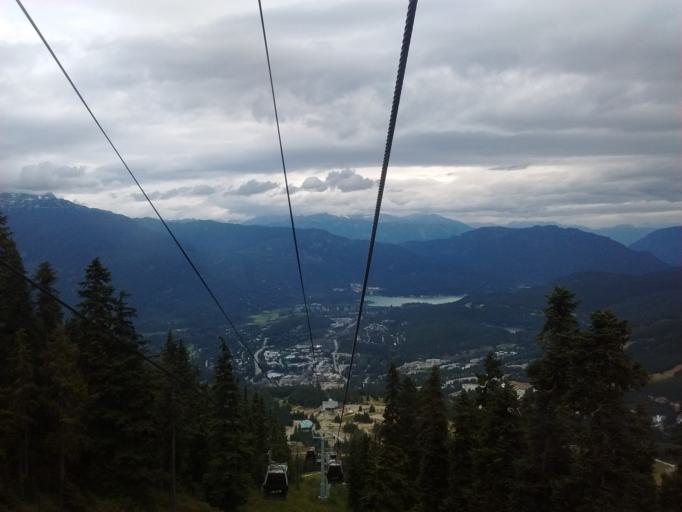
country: CA
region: British Columbia
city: Whistler
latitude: 50.0875
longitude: -122.9498
